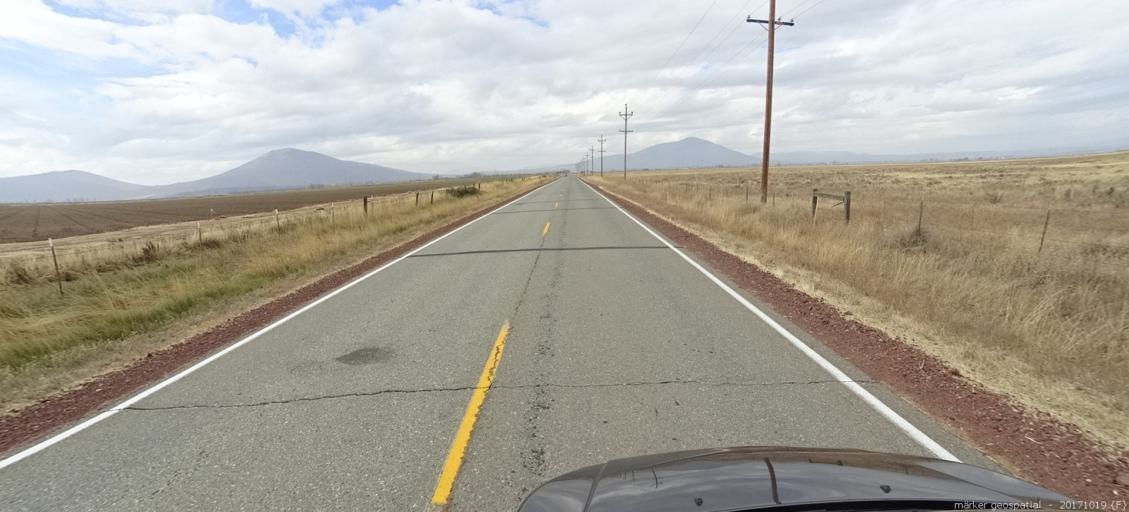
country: US
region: California
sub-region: Shasta County
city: Burney
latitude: 41.0509
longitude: -121.4182
